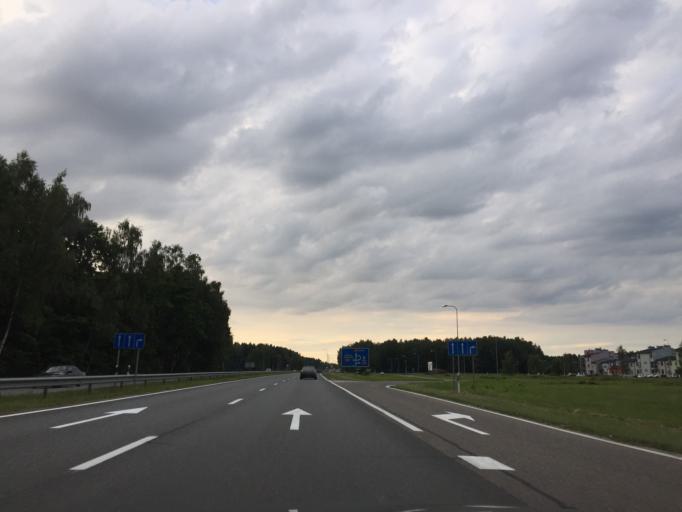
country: LV
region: Babite
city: Pinki
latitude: 56.9418
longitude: 23.9210
